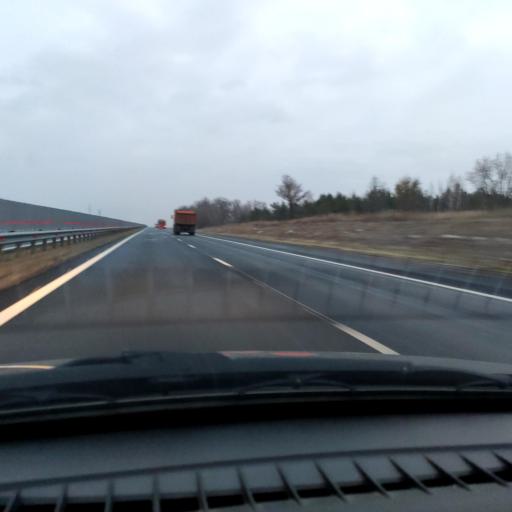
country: RU
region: Samara
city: Bereza
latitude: 53.4789
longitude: 50.1459
